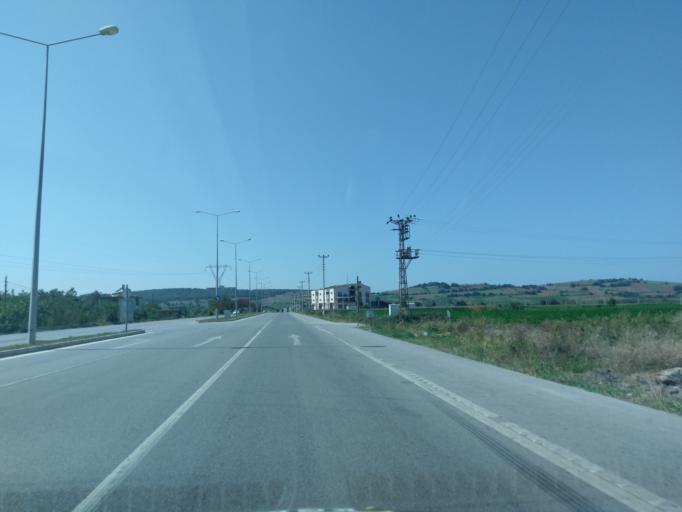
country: TR
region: Samsun
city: Bafra
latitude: 41.5751
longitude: 35.8616
